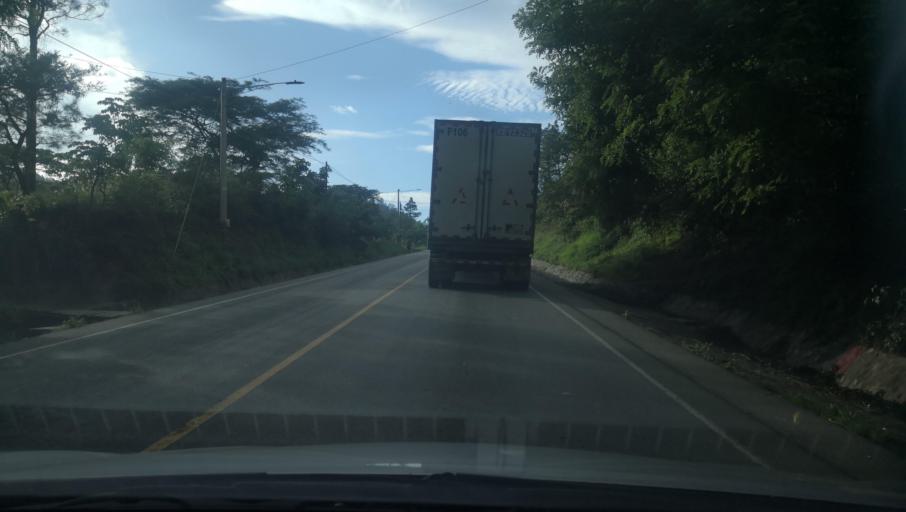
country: NI
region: Nueva Segovia
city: Mozonte
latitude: 13.7158
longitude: -86.5037
